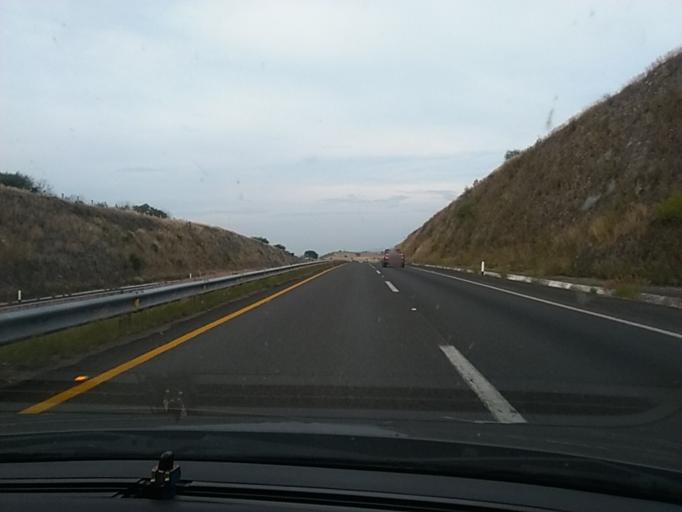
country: MX
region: Michoacan
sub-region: Zinapecuaro
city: Francisco Villa
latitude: 19.8841
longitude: -100.9225
